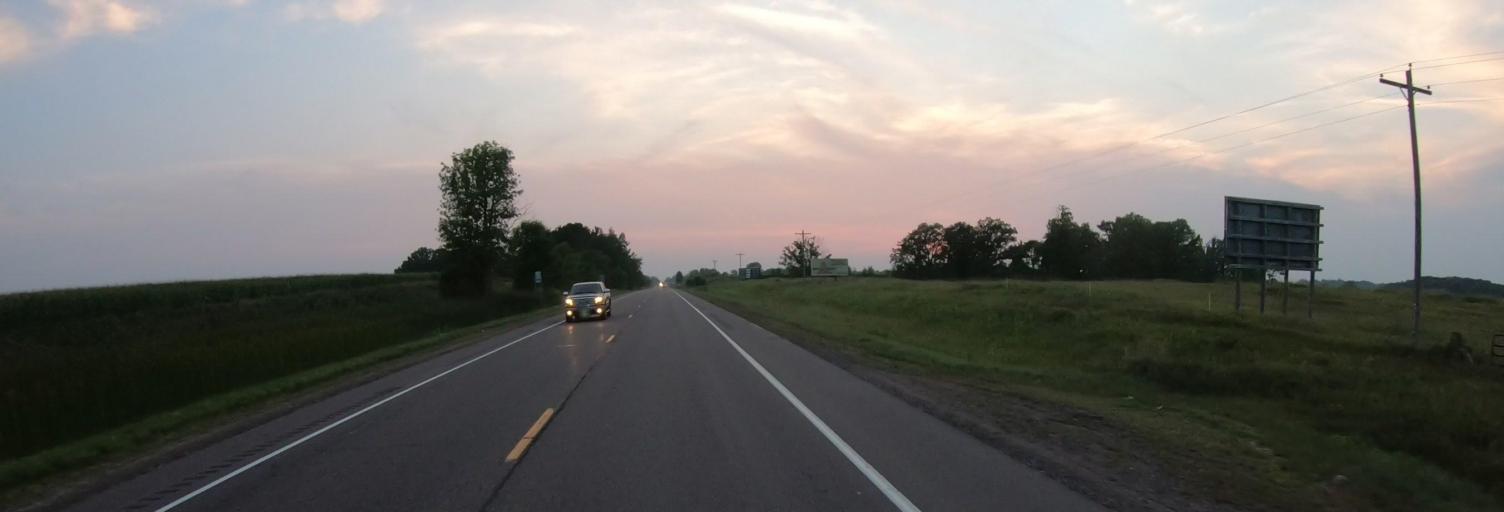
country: US
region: Minnesota
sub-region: Pine County
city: Rock Creek
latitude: 45.7666
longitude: -92.9732
